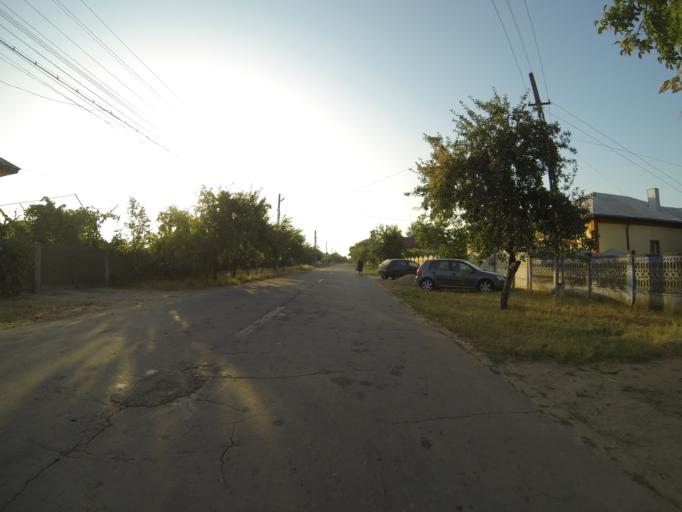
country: RO
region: Dolj
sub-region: Comuna Dobrotesti
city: Dobrotesti
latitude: 43.9615
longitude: 24.1160
